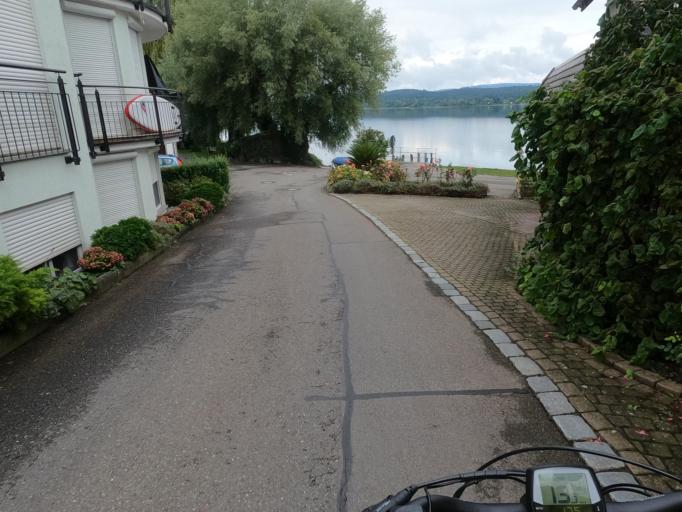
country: DE
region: Baden-Wuerttemberg
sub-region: Freiburg Region
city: Reichenau
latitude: 47.7068
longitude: 9.0463
